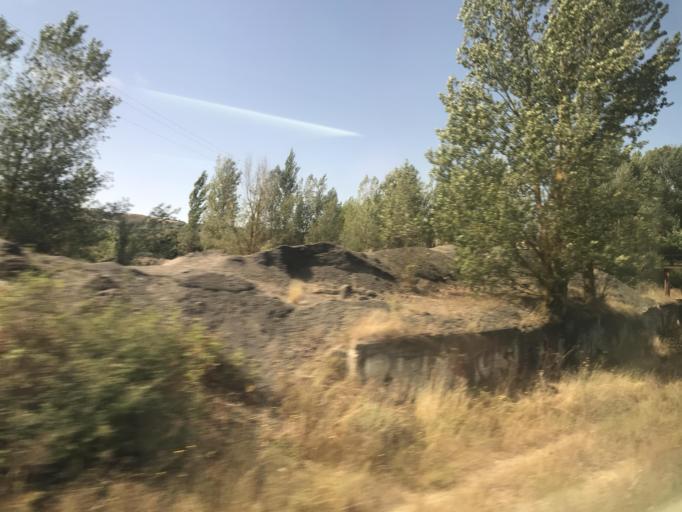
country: ES
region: Castille and Leon
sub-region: Provincia de Burgos
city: Quintanapalla
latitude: 42.4013
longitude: -3.5445
